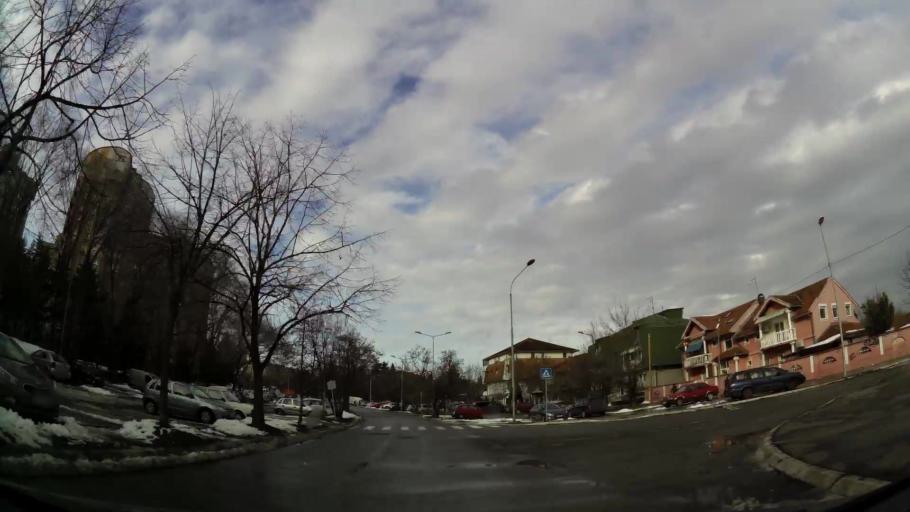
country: RS
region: Central Serbia
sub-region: Belgrade
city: Rakovica
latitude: 44.7400
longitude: 20.4260
